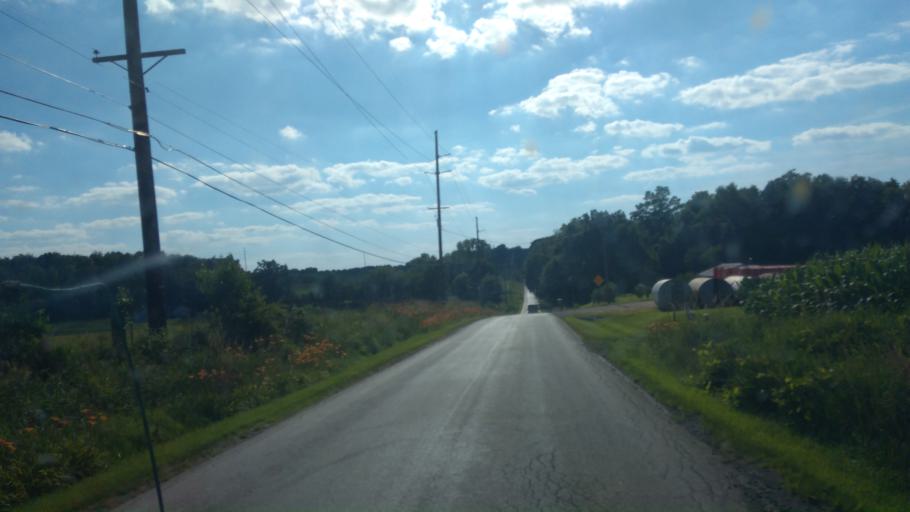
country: US
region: Ohio
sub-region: Wayne County
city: Shreve
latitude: 40.7118
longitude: -81.9590
